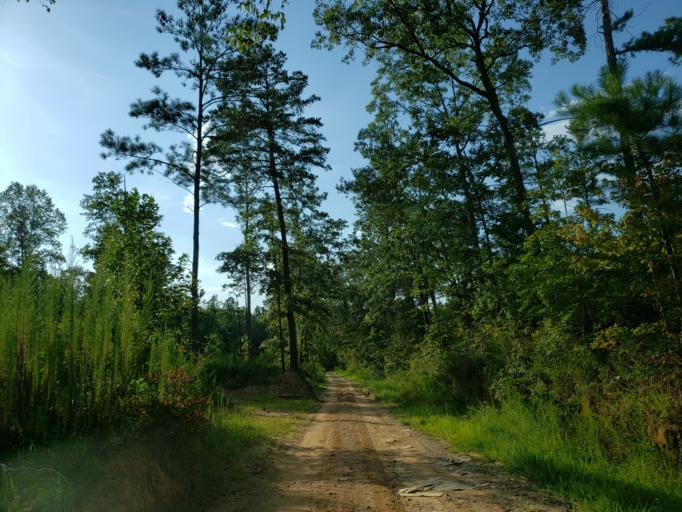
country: US
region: Georgia
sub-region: Cobb County
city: Acworth
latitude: 34.1675
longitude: -84.6426
